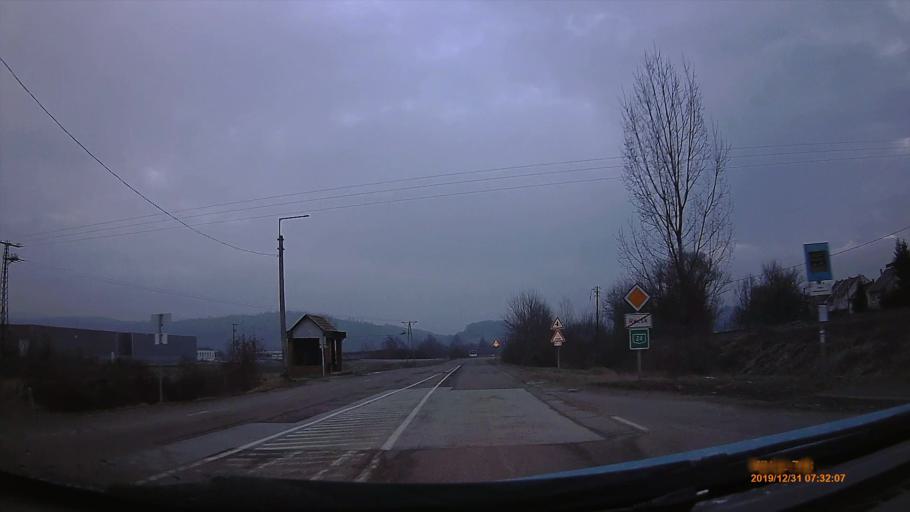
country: HU
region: Heves
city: Recsk
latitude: 47.9324
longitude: 20.1199
